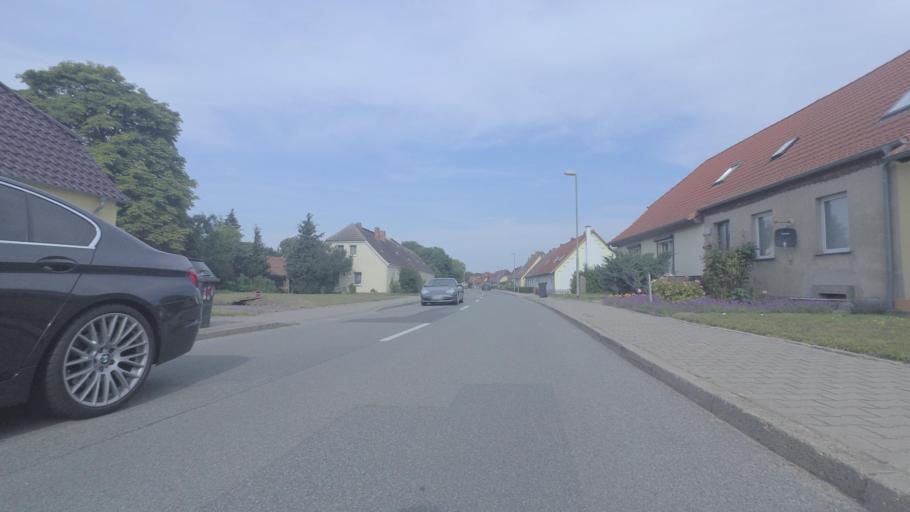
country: DE
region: Mecklenburg-Vorpommern
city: Gielow
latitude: 53.6488
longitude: 12.8293
